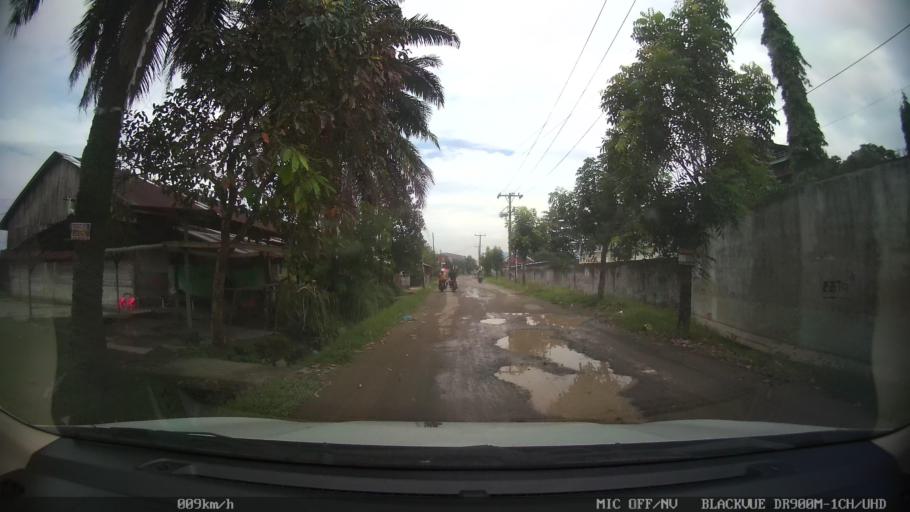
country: ID
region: North Sumatra
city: Sunggal
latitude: 3.6055
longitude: 98.6046
